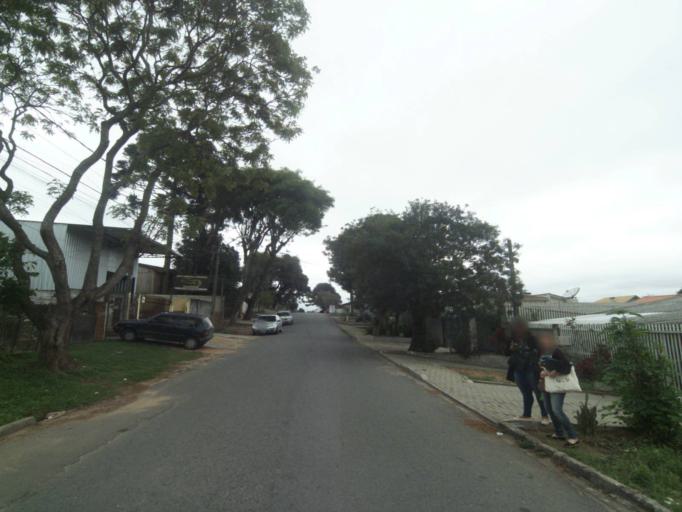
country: BR
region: Parana
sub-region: Sao Jose Dos Pinhais
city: Sao Jose dos Pinhais
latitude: -25.5419
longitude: -49.2930
